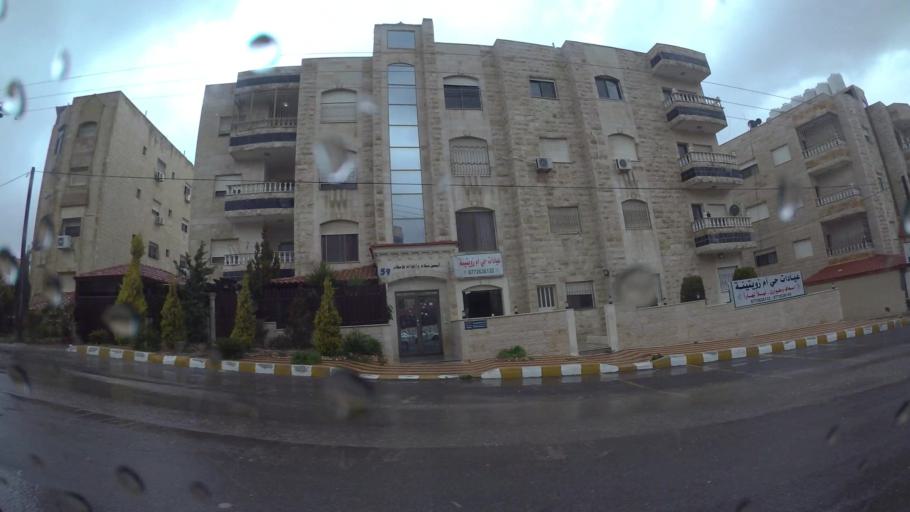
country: JO
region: Amman
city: Al Jubayhah
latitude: 32.0335
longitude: 35.8925
